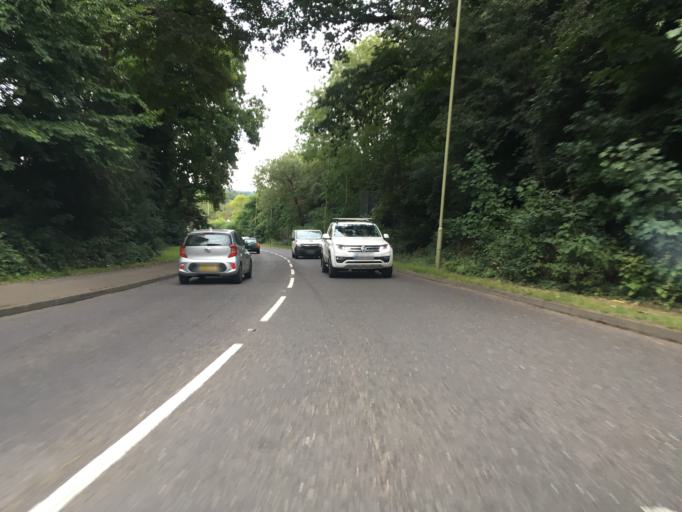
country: GB
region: England
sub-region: Hampshire
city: Petersfield
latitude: 51.0115
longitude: -0.9227
